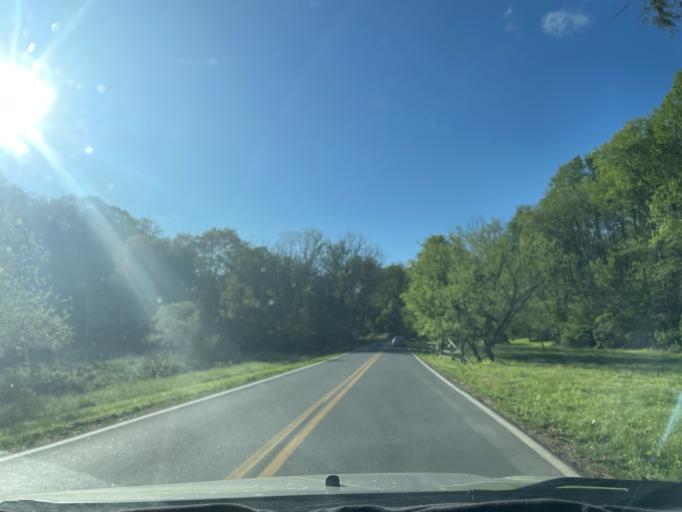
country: US
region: Maryland
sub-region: Carroll County
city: Mount Airy
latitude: 39.4195
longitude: -77.1460
